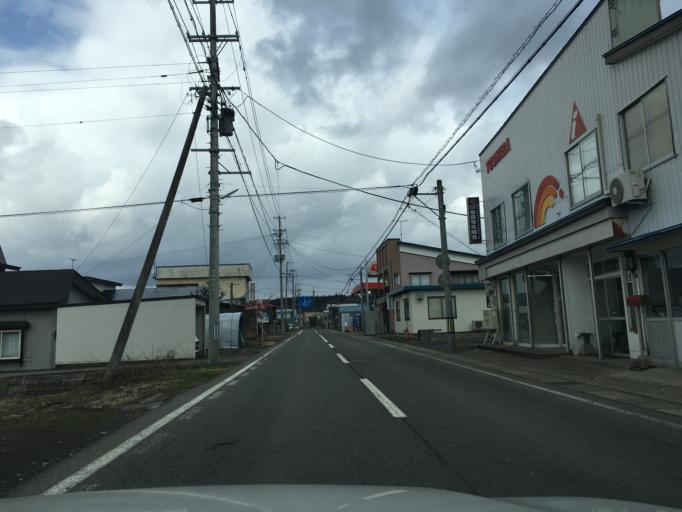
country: JP
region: Akita
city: Takanosu
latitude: 40.1566
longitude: 140.3342
